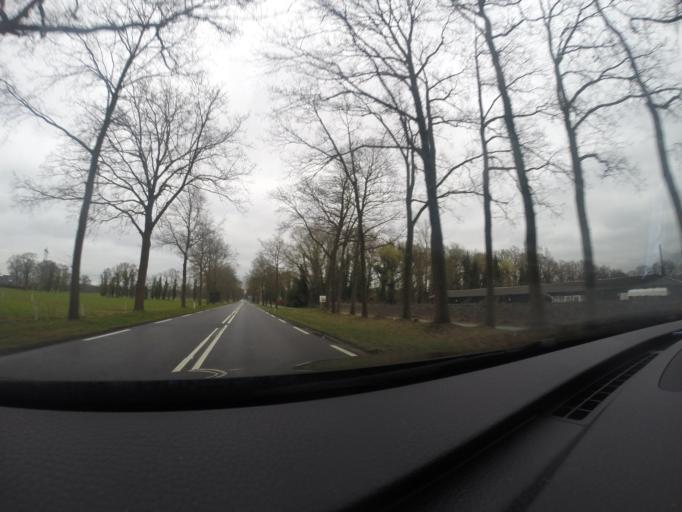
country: NL
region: Overijssel
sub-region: Gemeente Hof van Twente
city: Delden
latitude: 52.2419
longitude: 6.6933
